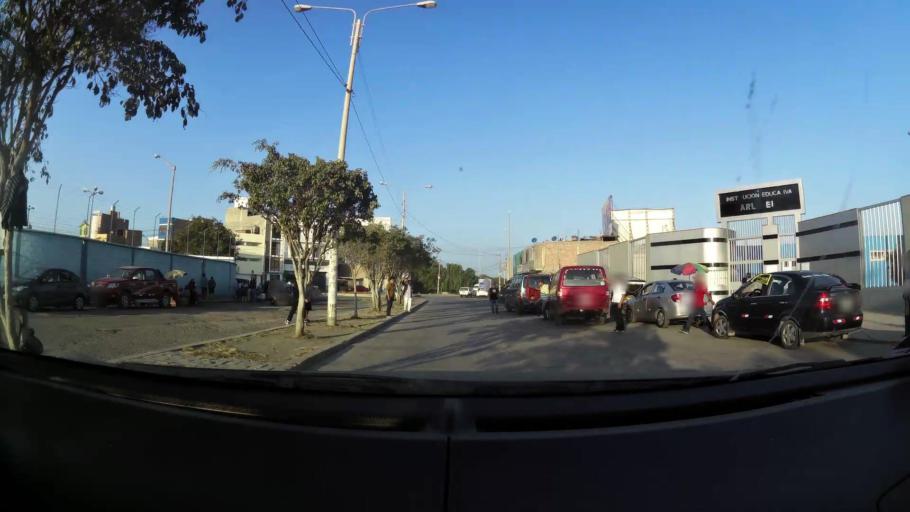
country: PE
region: Lambayeque
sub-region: Provincia de Chiclayo
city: Santa Rosa
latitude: -6.7743
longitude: -79.8299
